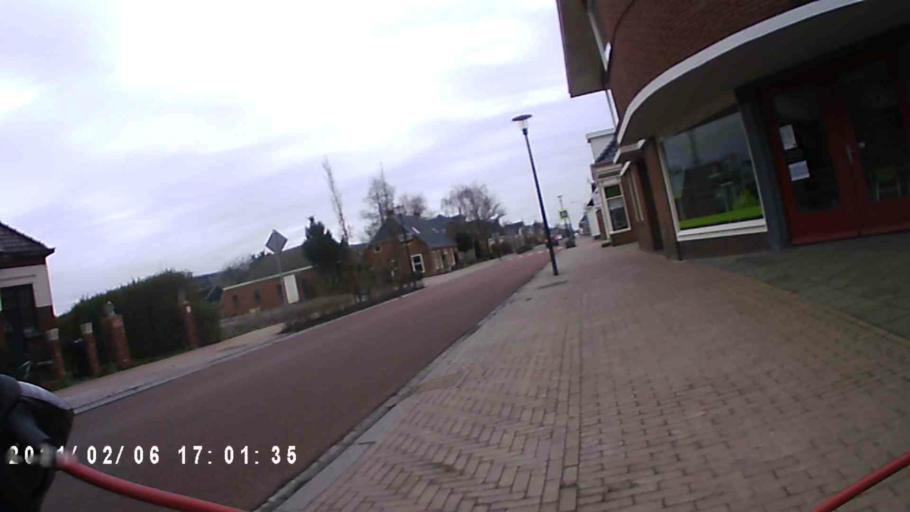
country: NL
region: Groningen
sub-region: Gemeente Appingedam
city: Appingedam
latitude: 53.4204
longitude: 6.7633
